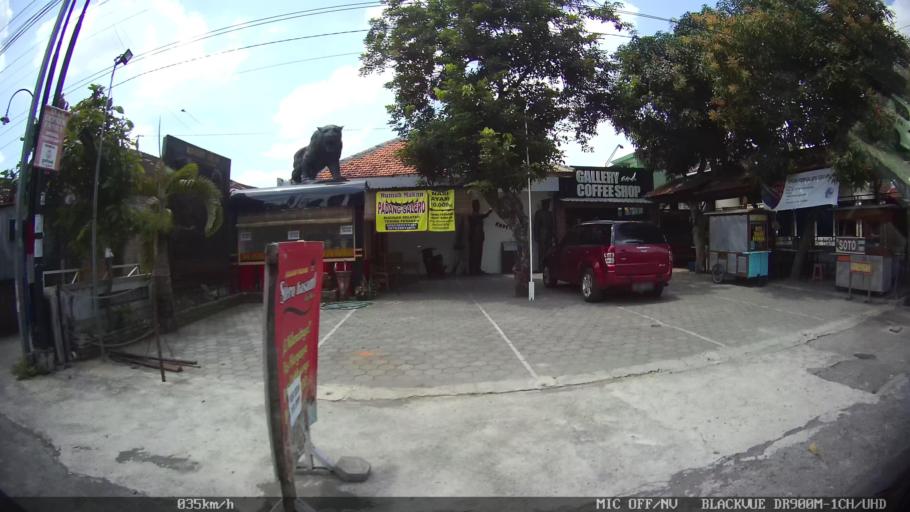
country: ID
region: Daerah Istimewa Yogyakarta
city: Kasihan
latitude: -7.8194
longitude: 110.3481
